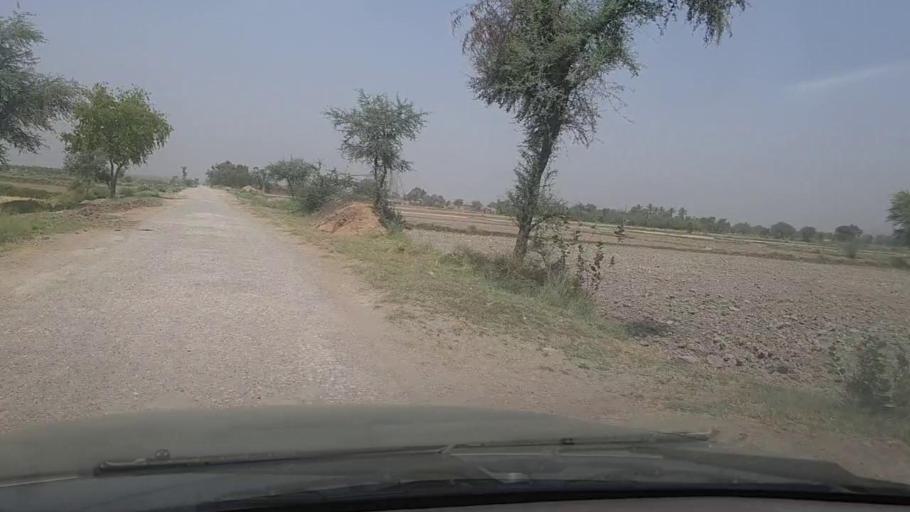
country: PK
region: Sindh
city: Madeji
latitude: 27.7966
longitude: 68.4529
